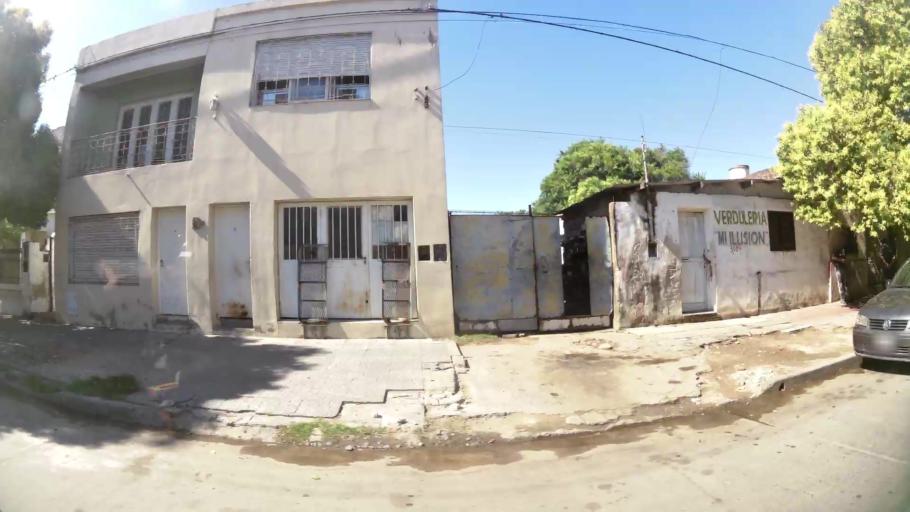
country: AR
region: Cordoba
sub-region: Departamento de Capital
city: Cordoba
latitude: -31.4354
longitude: -64.1467
